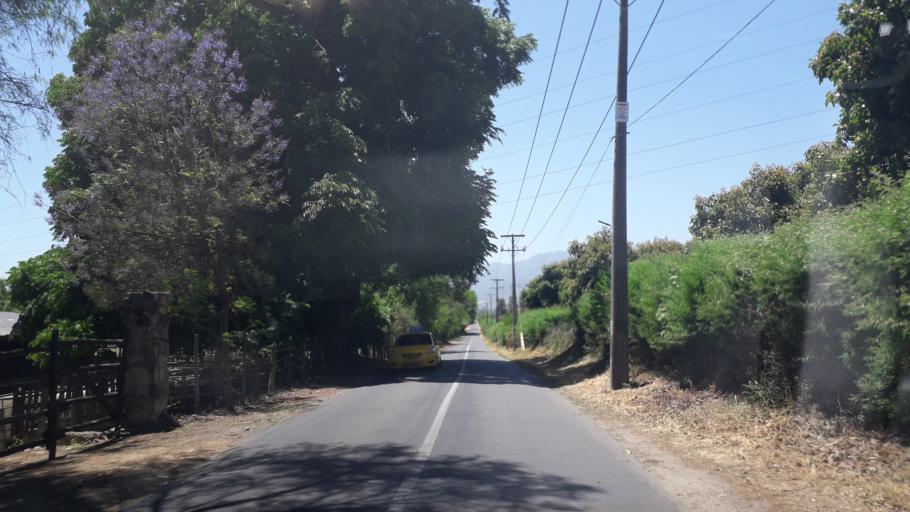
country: CL
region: Valparaiso
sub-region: Provincia de Quillota
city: Quillota
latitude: -32.9300
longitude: -71.2561
